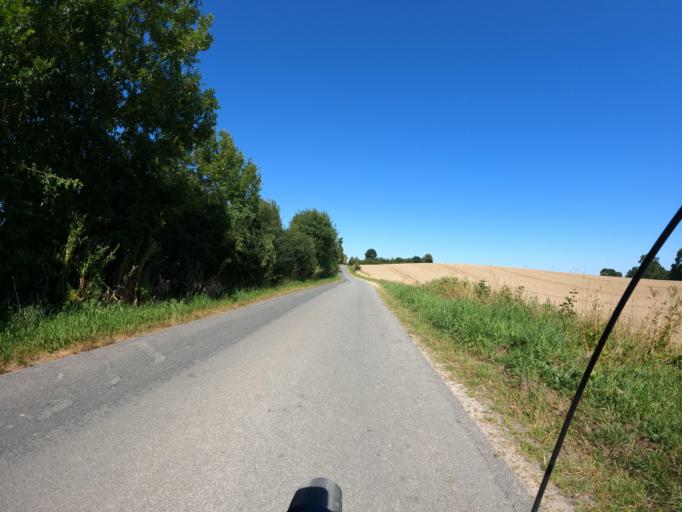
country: DE
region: Schleswig-Holstein
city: Steinbergkirche
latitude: 54.7932
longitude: 9.7443
